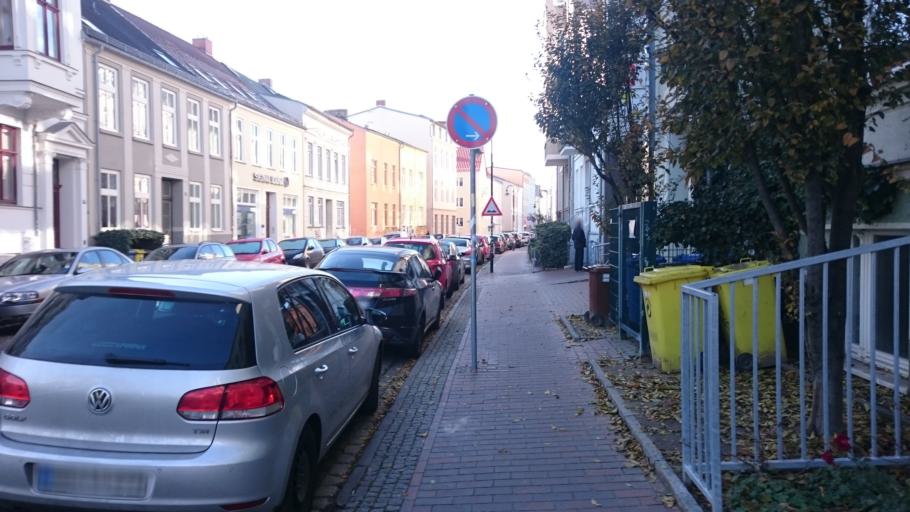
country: DE
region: Mecklenburg-Vorpommern
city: Rostock
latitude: 54.0840
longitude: 12.1329
